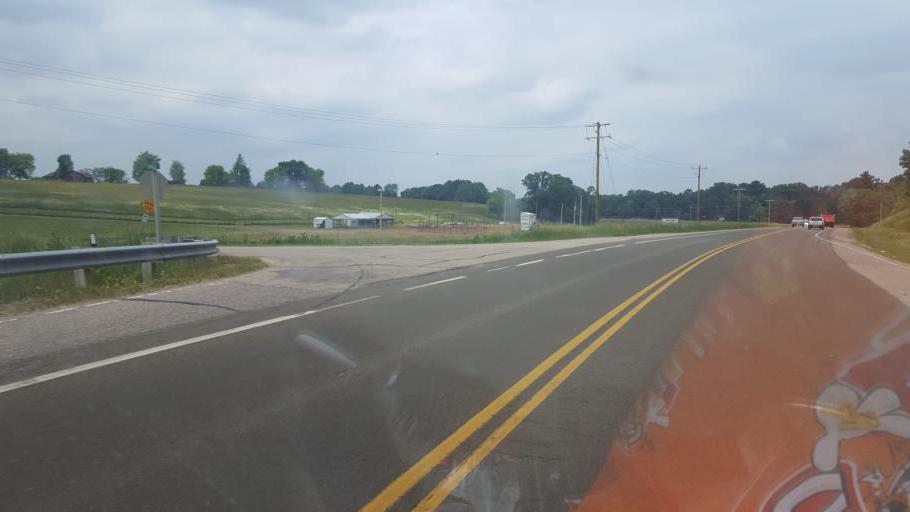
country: US
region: Wisconsin
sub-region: Sauk County
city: Reedsburg
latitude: 43.5694
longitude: -90.0998
